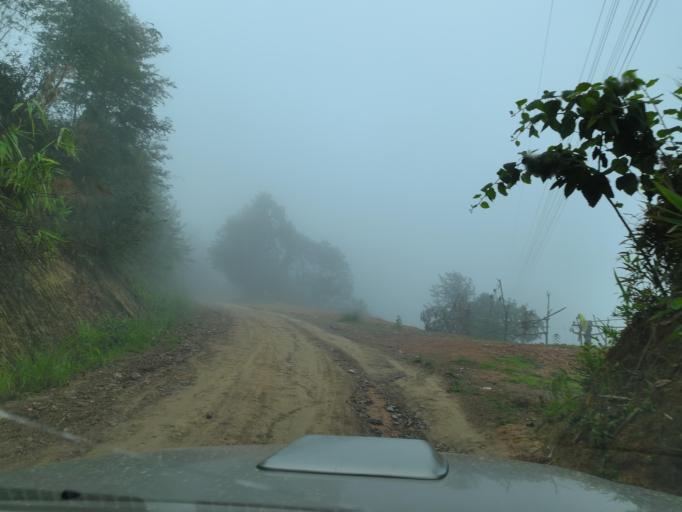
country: LA
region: Phongsali
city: Phongsali
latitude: 21.6459
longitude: 102.1119
